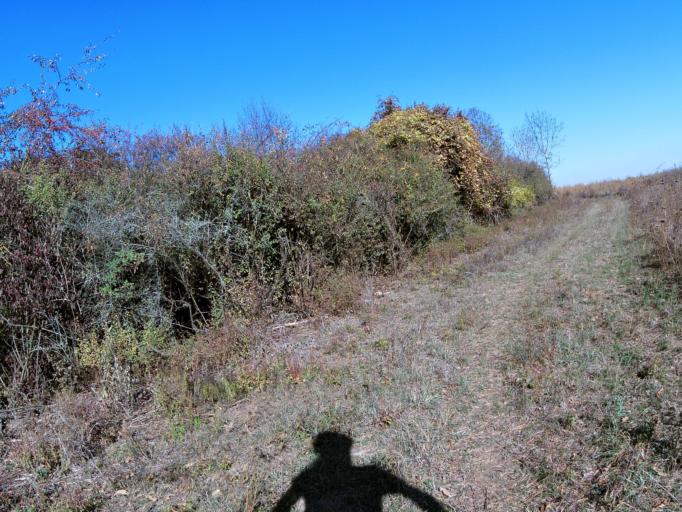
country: DE
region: Bavaria
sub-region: Regierungsbezirk Unterfranken
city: Eibelstadt
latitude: 49.7140
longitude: 9.9838
